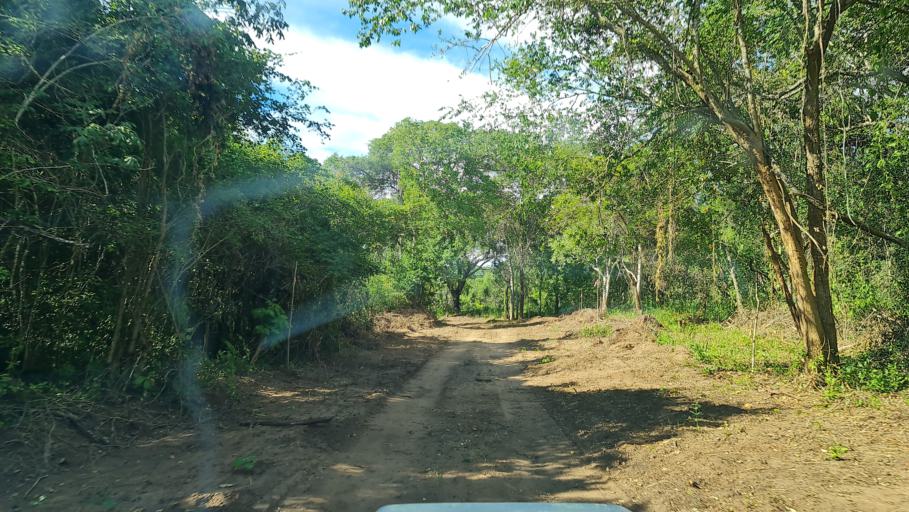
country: MZ
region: Nampula
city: Antonio Enes
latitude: -15.5278
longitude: 40.1268
